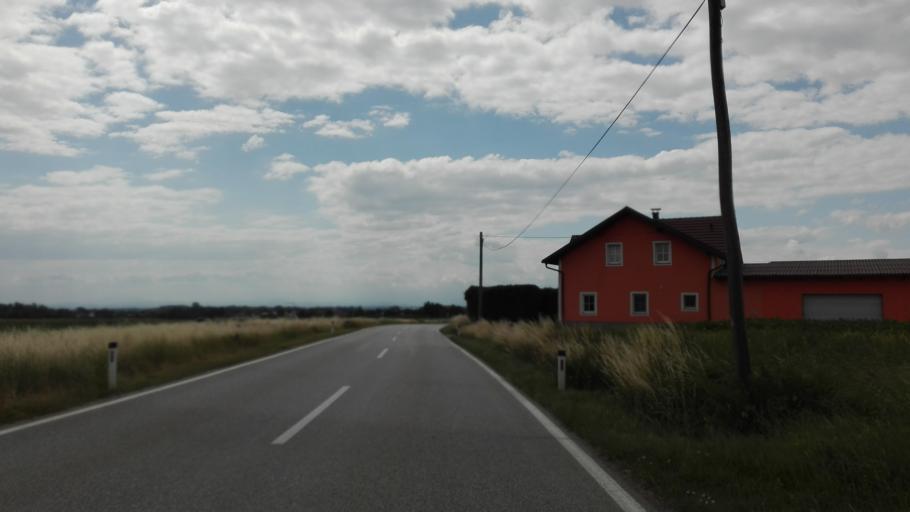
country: AT
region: Lower Austria
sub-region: Politischer Bezirk Amstetten
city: Ennsdorf
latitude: 48.2549
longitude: 14.5403
